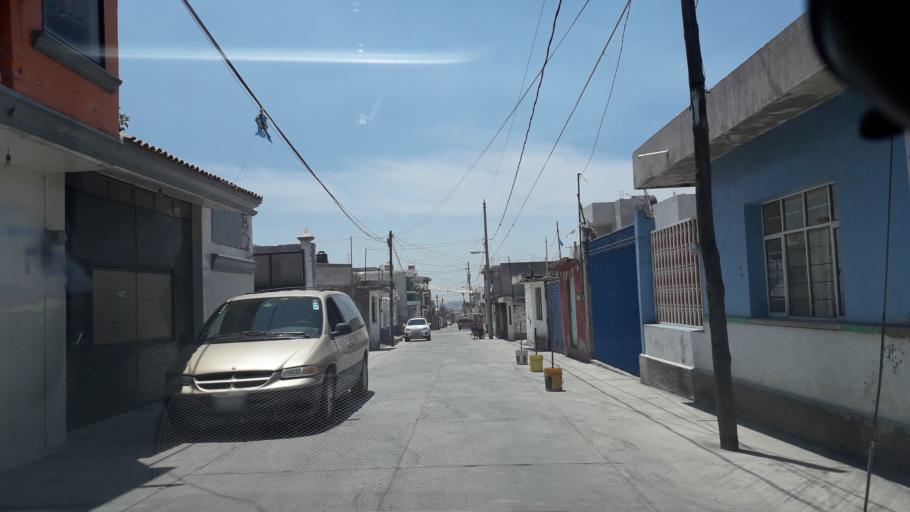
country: MX
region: Puebla
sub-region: Puebla
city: Santa Maria Xonacatepec
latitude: 19.0882
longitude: -98.1063
